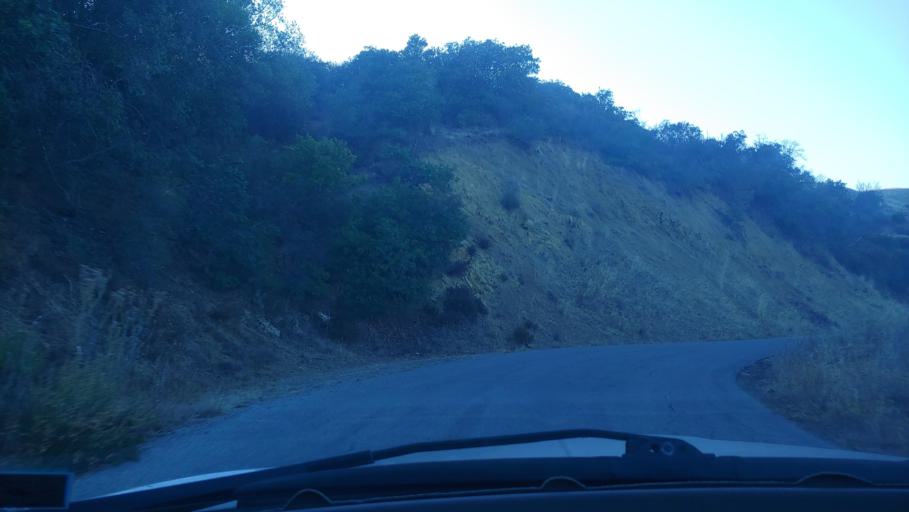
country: US
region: California
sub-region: Santa Barbara County
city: Goleta
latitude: 34.5164
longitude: -119.7930
